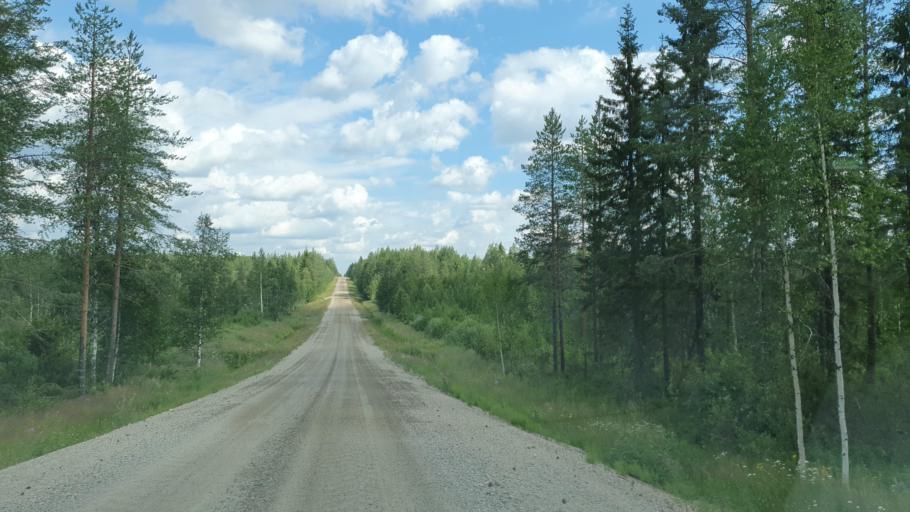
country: FI
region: Kainuu
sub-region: Kehys-Kainuu
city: Kuhmo
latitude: 64.4837
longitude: 29.5925
